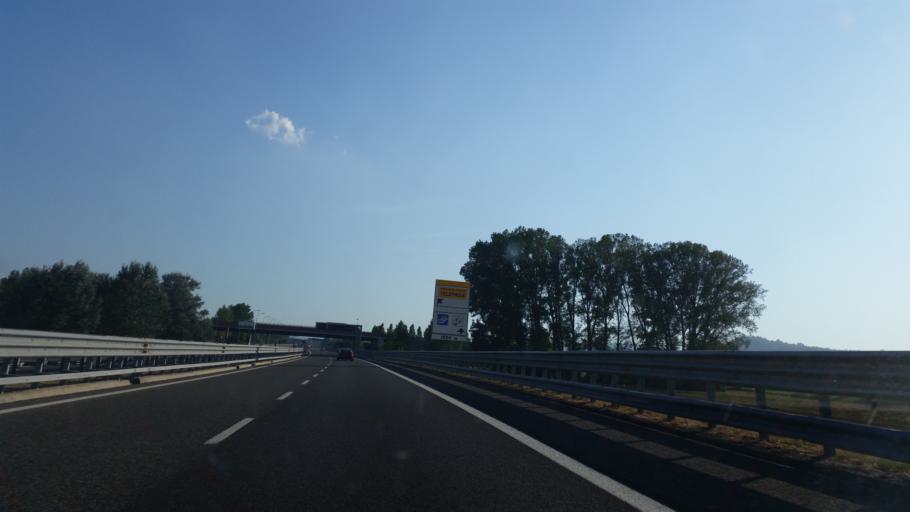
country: IT
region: Piedmont
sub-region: Provincia di Cuneo
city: Govone
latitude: 44.7795
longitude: 8.1120
